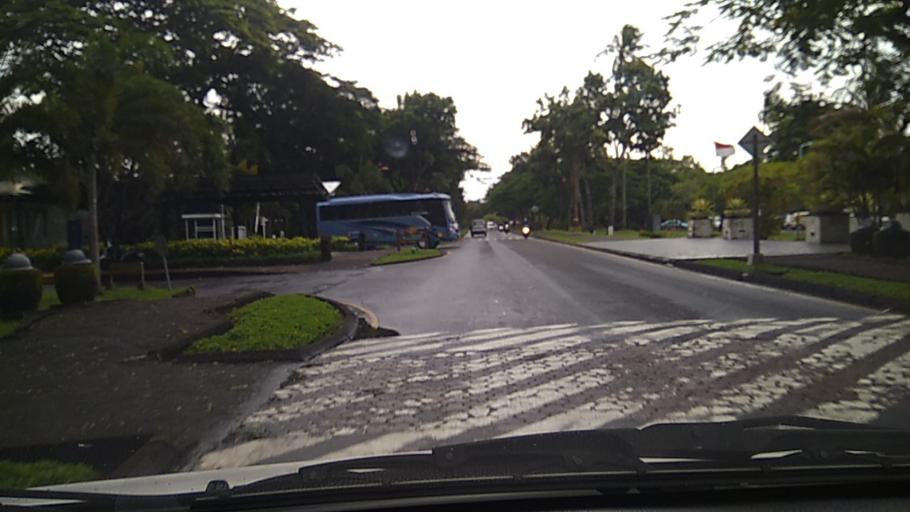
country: ID
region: Bali
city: Bualu
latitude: -8.8017
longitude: 115.2288
